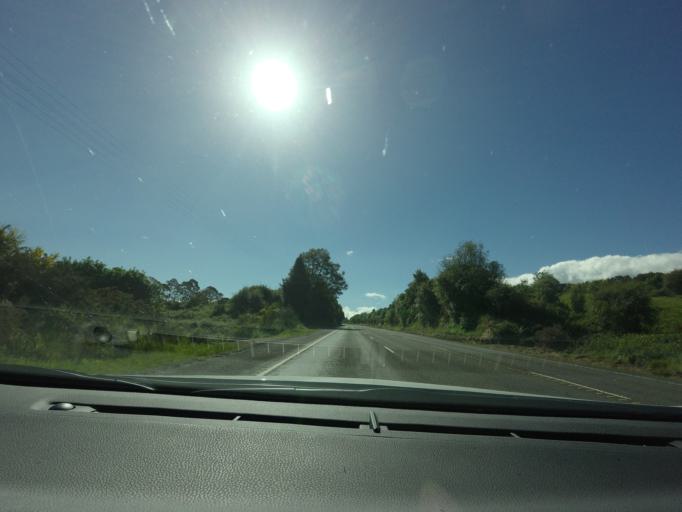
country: NZ
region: Bay of Plenty
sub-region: Rotorua District
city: Rotorua
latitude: -38.0746
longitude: 176.1782
